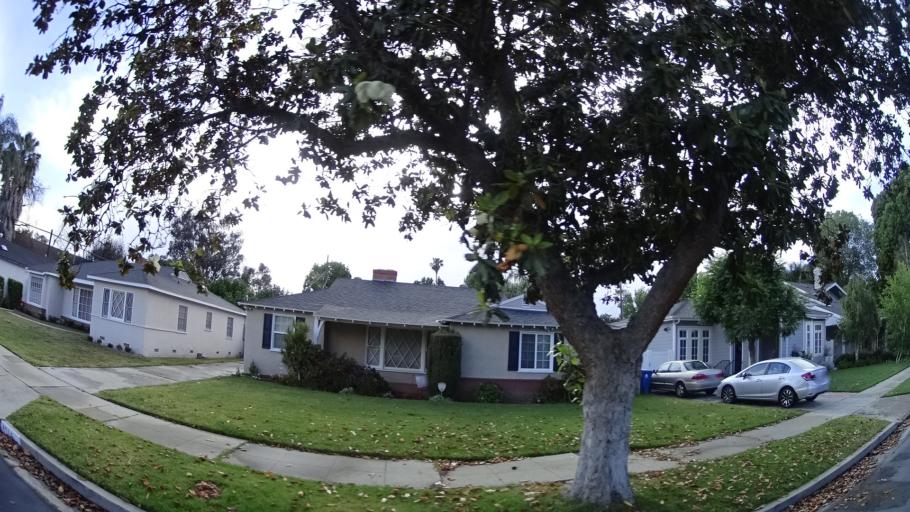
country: US
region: California
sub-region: Los Angeles County
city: Sherman Oaks
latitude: 34.1563
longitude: -118.4279
